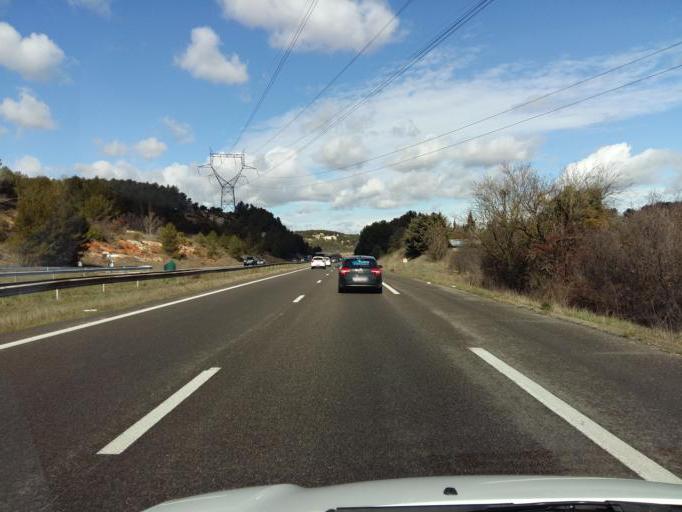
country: FR
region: Provence-Alpes-Cote d'Azur
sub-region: Departement des Bouches-du-Rhone
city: Cabries
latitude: 43.4422
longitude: 5.3963
